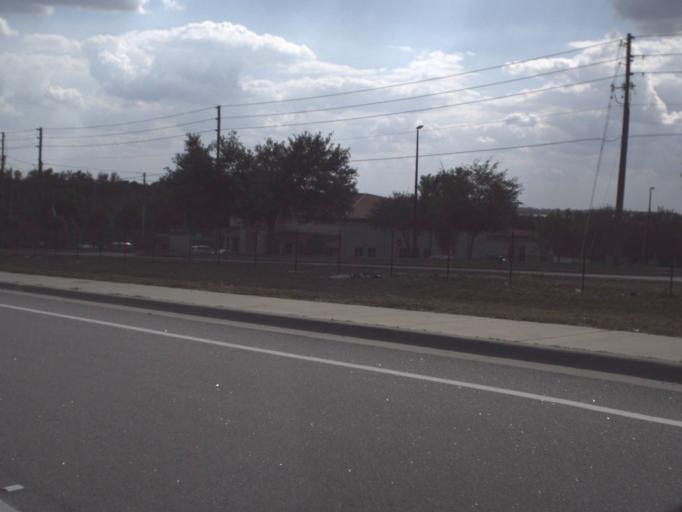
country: US
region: Florida
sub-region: Lake County
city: Minneola
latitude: 28.5444
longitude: -81.7421
